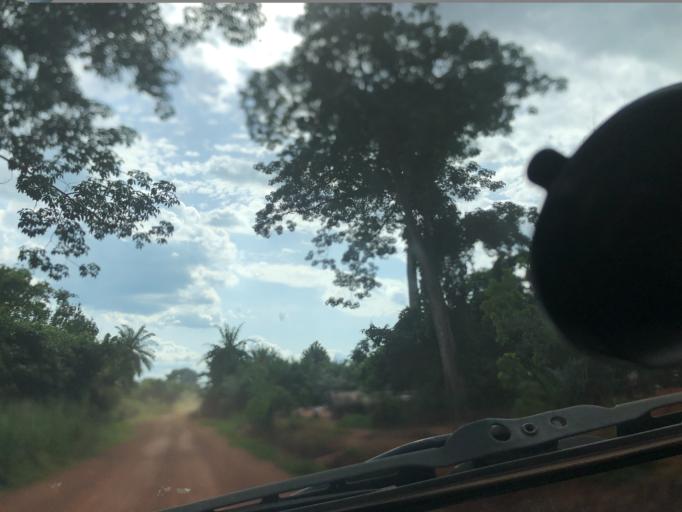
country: CF
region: Bangui
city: Bangui
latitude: 4.2174
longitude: 18.6881
